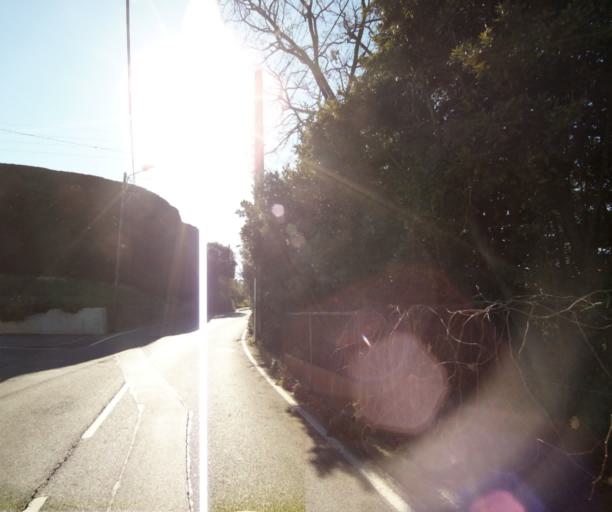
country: FR
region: Provence-Alpes-Cote d'Azur
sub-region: Departement des Alpes-Maritimes
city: Antibes
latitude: 43.5915
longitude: 7.1106
